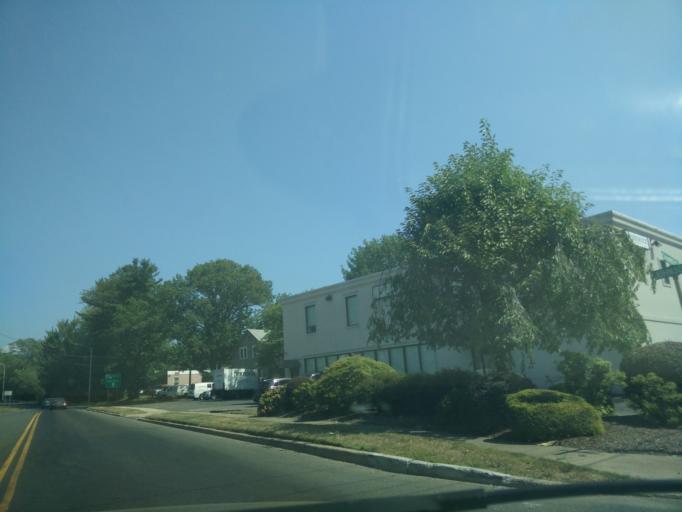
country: US
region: Connecticut
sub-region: Fairfield County
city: Bridgeport
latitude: 41.1658
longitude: -73.2324
